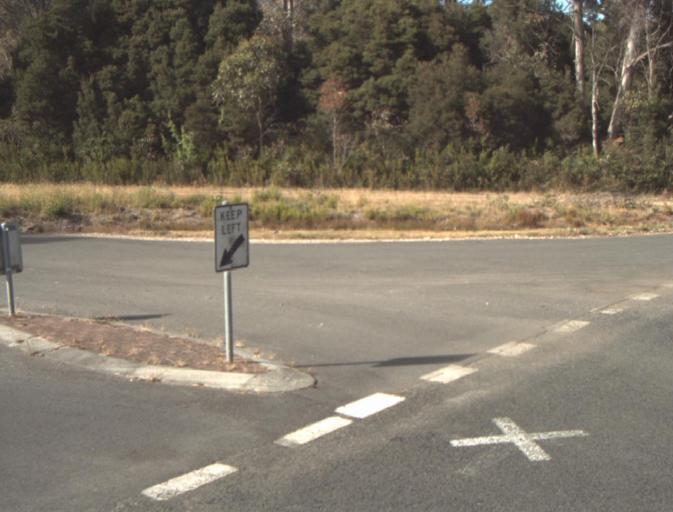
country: AU
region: Tasmania
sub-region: Launceston
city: Mayfield
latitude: -41.3121
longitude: 147.1990
